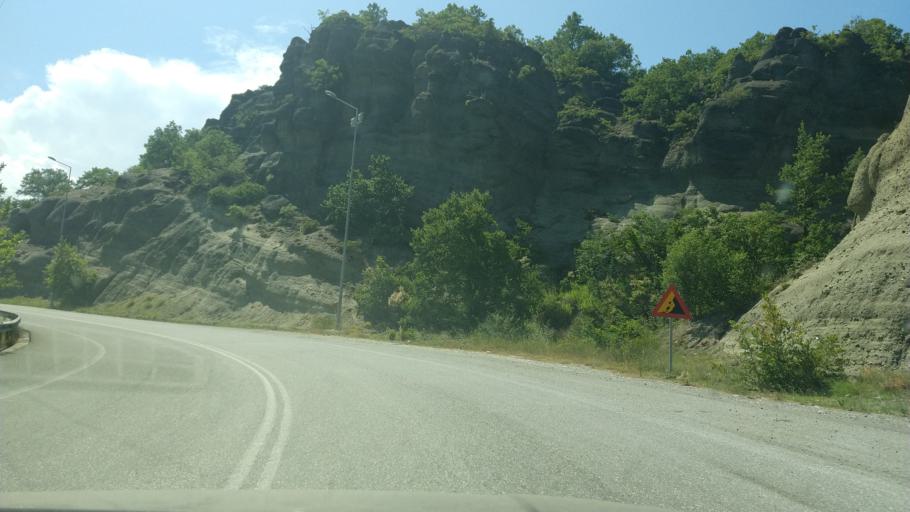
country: GR
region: West Macedonia
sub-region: Nomos Grevenon
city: Grevena
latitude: 40.0519
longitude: 21.4803
